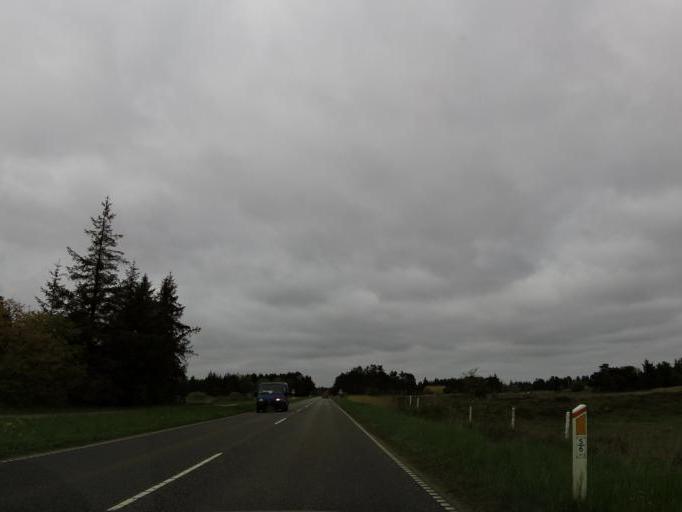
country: DE
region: Schleswig-Holstein
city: List
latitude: 55.1027
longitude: 8.5423
